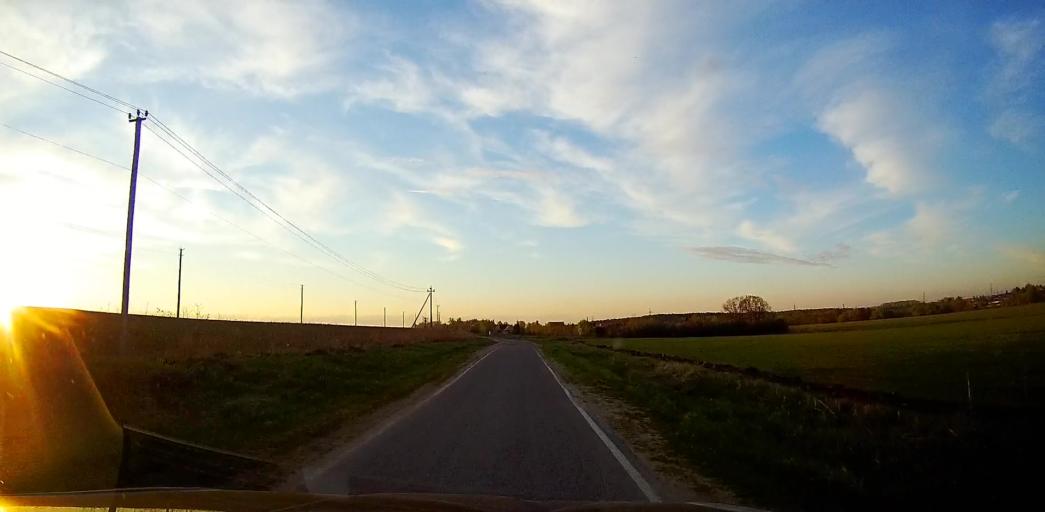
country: RU
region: Moskovskaya
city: Peski
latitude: 55.2238
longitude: 38.7360
